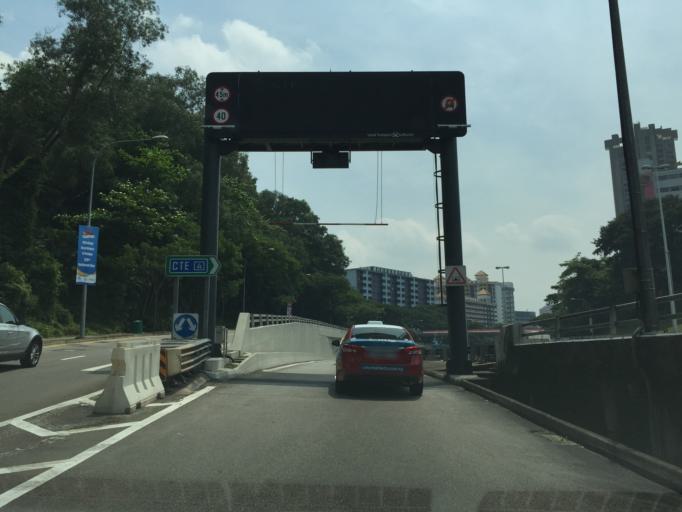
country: SG
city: Singapore
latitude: 1.2844
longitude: 103.8368
